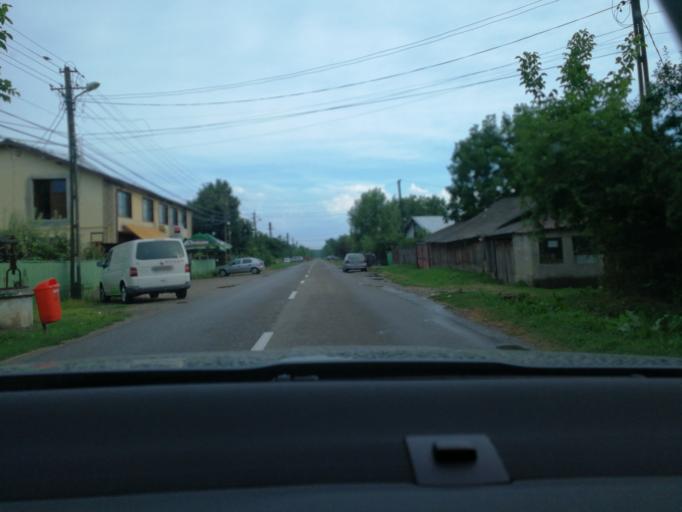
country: RO
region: Prahova
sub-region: Comuna Ceptura
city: Ceptura de Jos
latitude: 45.0119
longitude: 26.3349
